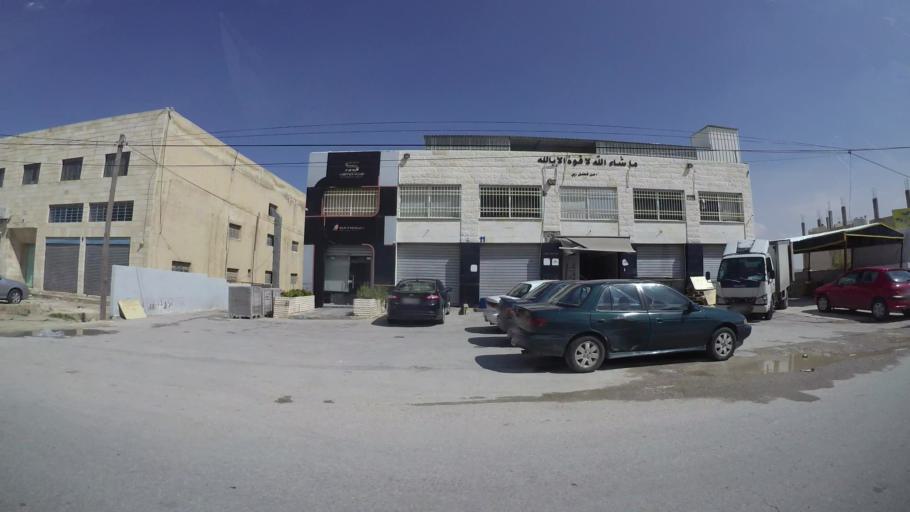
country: JO
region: Zarqa
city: Russeifa
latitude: 31.9928
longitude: 36.0071
